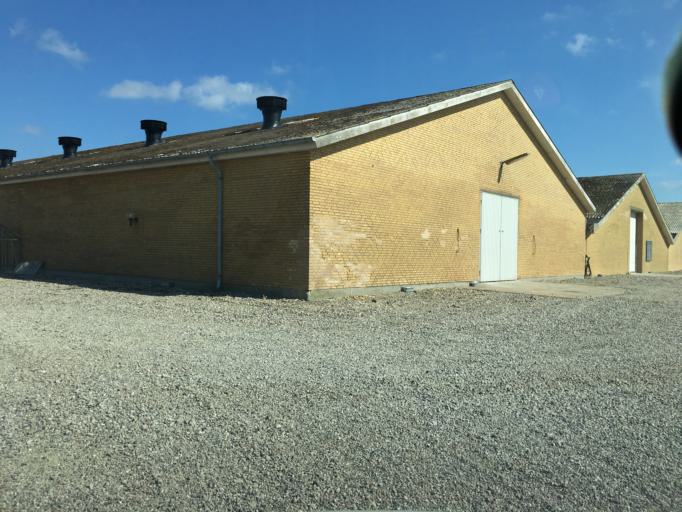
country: DK
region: South Denmark
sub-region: Sonderborg Kommune
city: Dybbol
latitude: 54.9604
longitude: 9.7337
